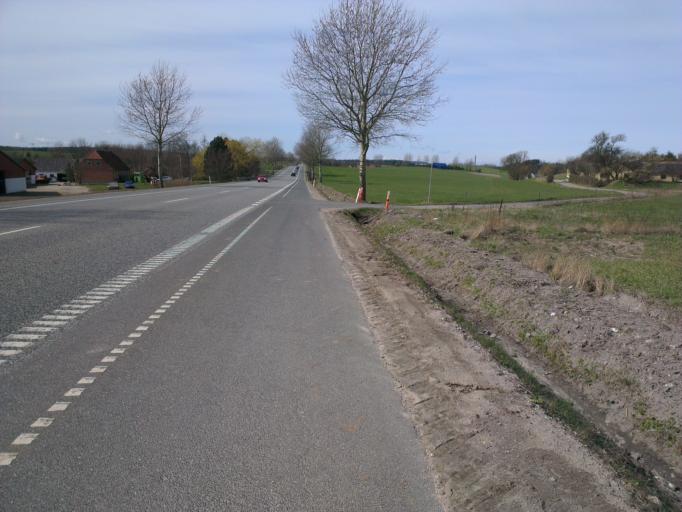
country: DK
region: Capital Region
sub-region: Frederikssund Kommune
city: Frederikssund
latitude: 55.8462
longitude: 12.1136
